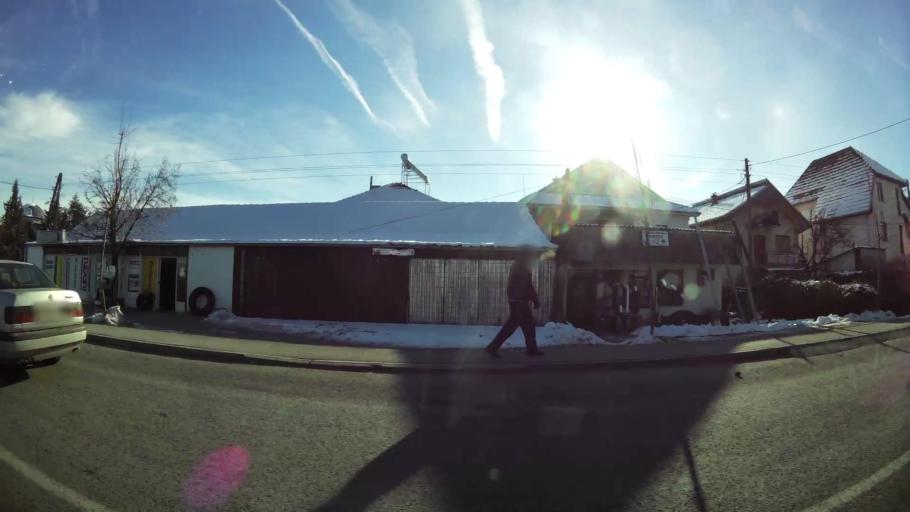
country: MK
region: Saraj
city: Saraj
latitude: 42.0013
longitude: 21.3302
